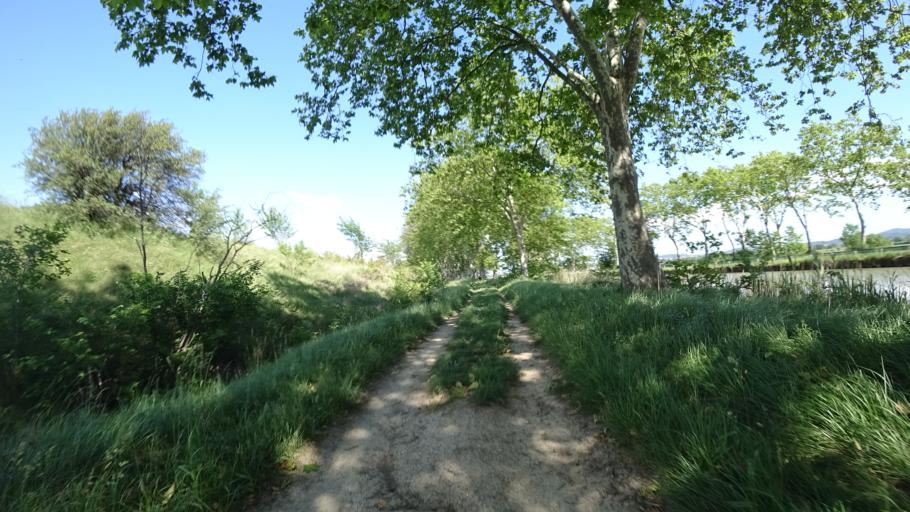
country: FR
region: Languedoc-Roussillon
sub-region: Departement de l'Aude
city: Ginestas
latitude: 43.2482
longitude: 2.8691
